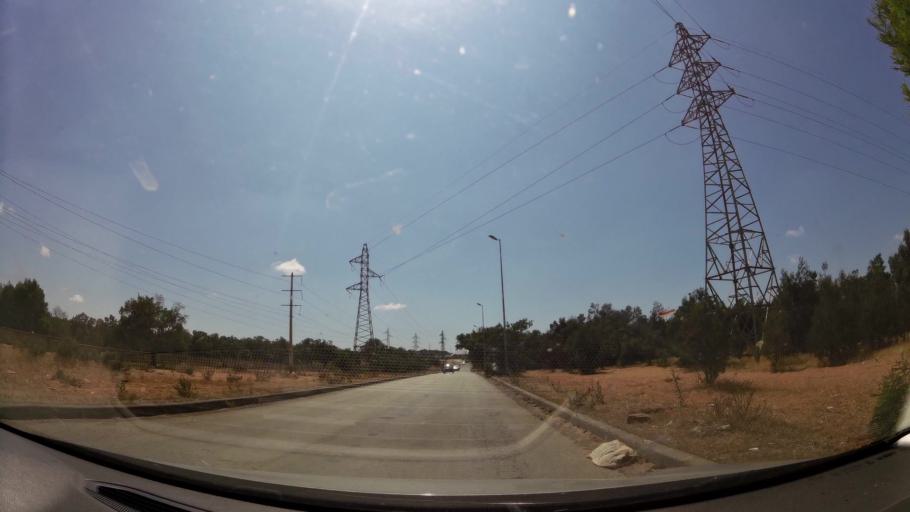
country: MA
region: Gharb-Chrarda-Beni Hssen
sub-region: Kenitra Province
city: Kenitra
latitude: 34.2367
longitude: -6.5666
